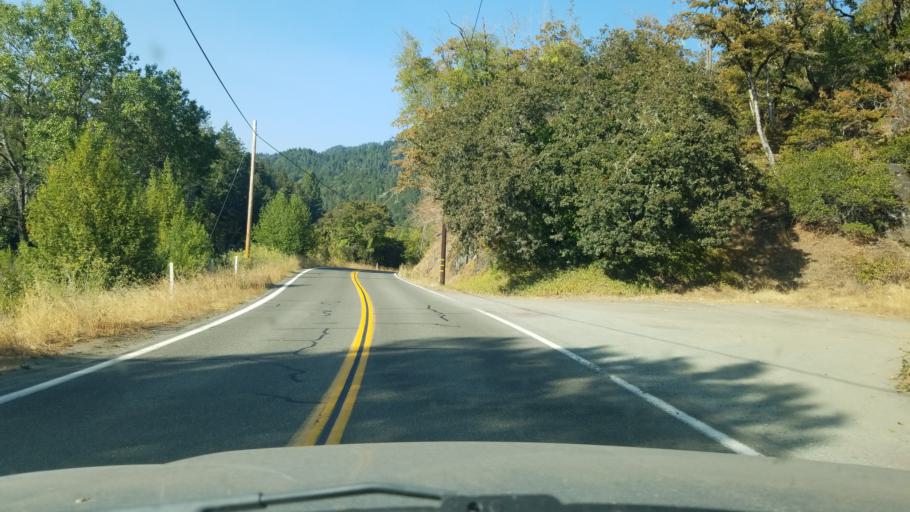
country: US
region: California
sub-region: Humboldt County
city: Redway
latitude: 40.1867
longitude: -123.7710
